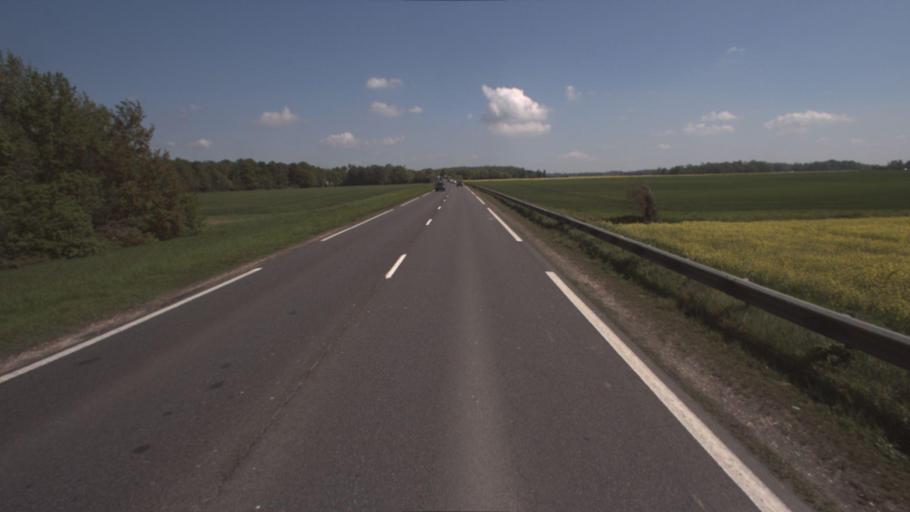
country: FR
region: Ile-de-France
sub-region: Departement de Seine-et-Marne
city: Fontenay-Tresigny
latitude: 48.7112
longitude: 2.8409
